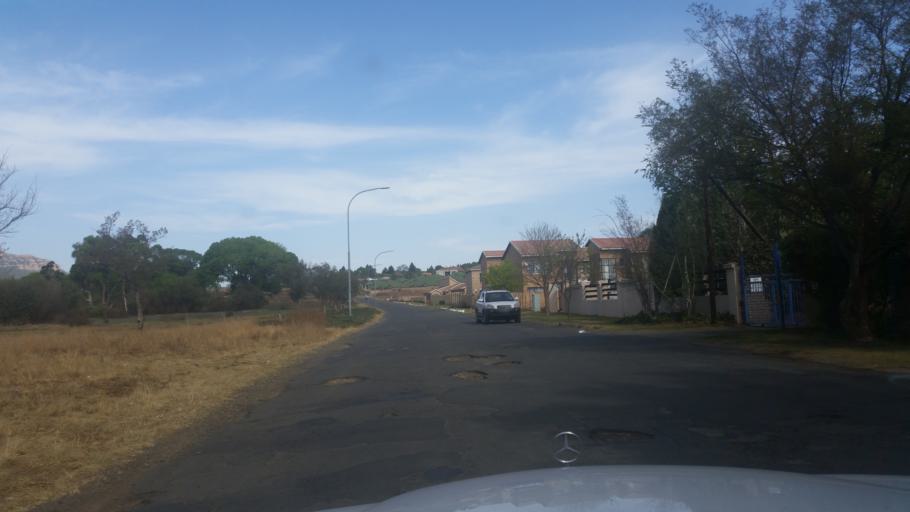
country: ZA
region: Orange Free State
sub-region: Thabo Mofutsanyana District Municipality
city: Harrismith
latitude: -28.2675
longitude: 29.1374
